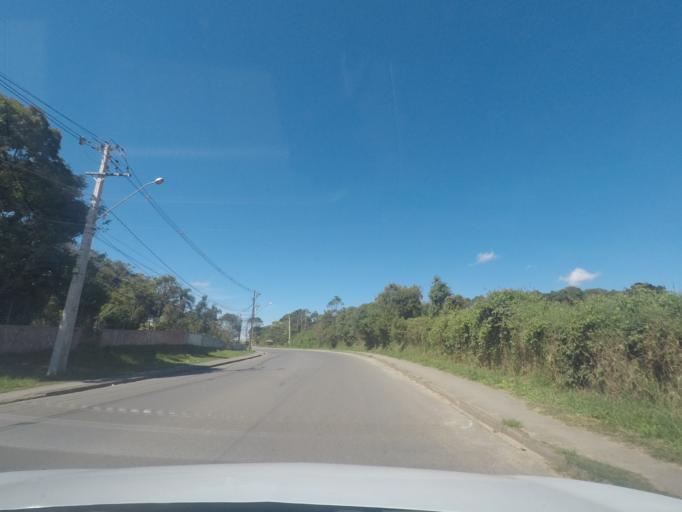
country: BR
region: Parana
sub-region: Almirante Tamandare
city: Almirante Tamandare
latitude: -25.3433
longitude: -49.3007
